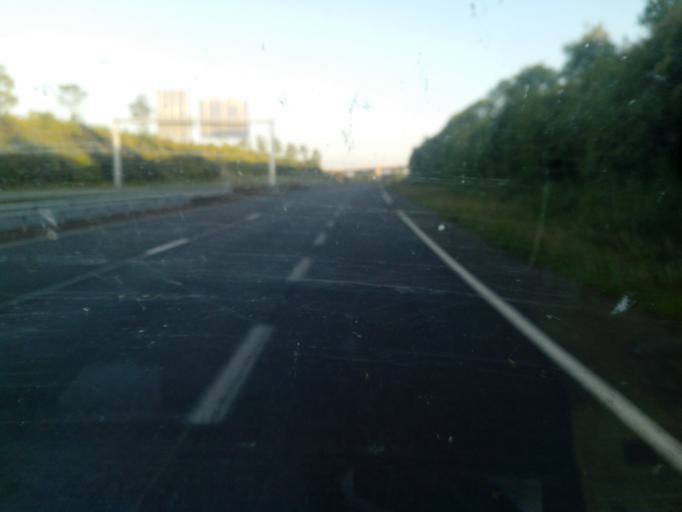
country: FR
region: Lower Normandy
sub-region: Departement de la Manche
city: Saint-Quentin-sur-le-Homme
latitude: 48.6207
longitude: -1.3357
